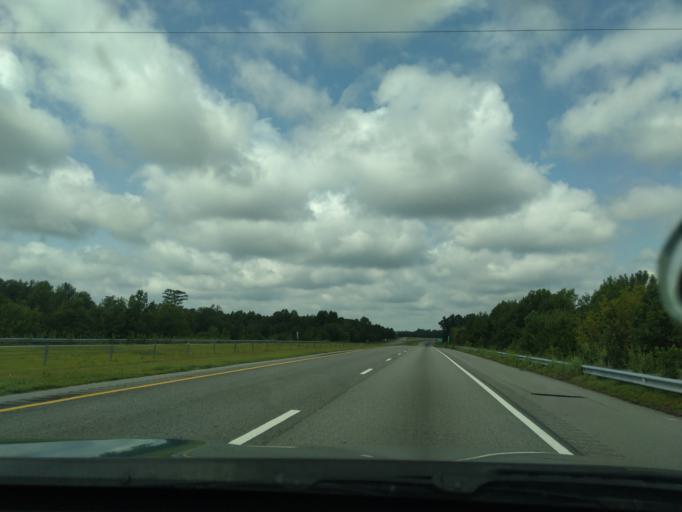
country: US
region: North Carolina
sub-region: Martin County
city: Robersonville
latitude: 35.8269
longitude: -77.1708
